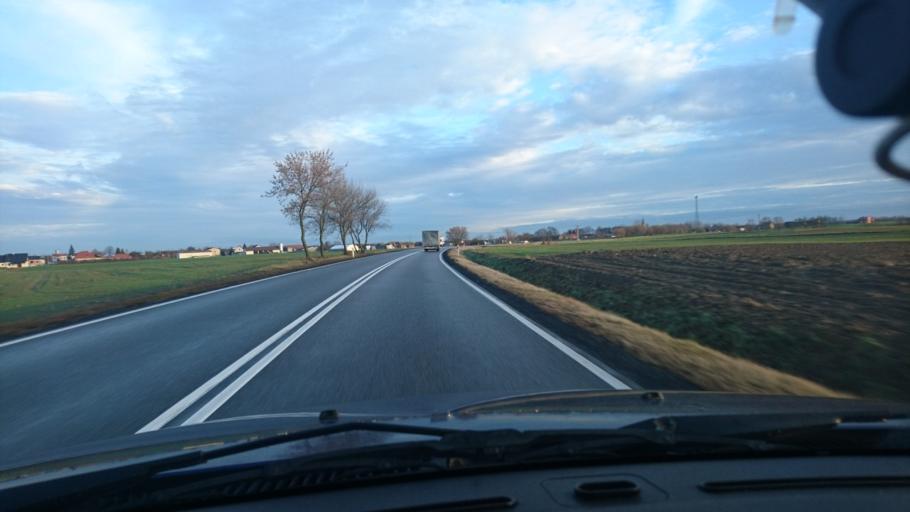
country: PL
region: Greater Poland Voivodeship
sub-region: Powiat kepinski
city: Opatow
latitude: 51.2208
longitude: 18.1335
